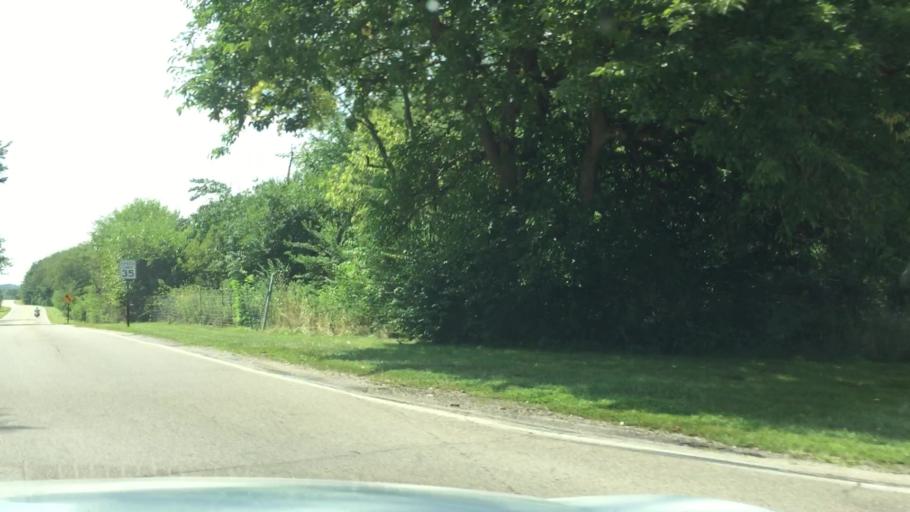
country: US
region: Ohio
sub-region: Clark County
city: Northridge
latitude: 39.9460
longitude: -83.7296
